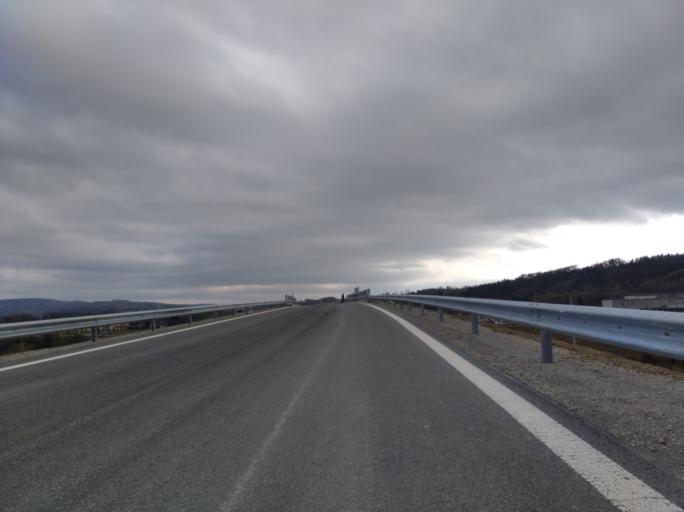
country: PL
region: Subcarpathian Voivodeship
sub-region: Powiat strzyzowski
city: Strzyzow
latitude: 49.8695
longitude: 21.7682
